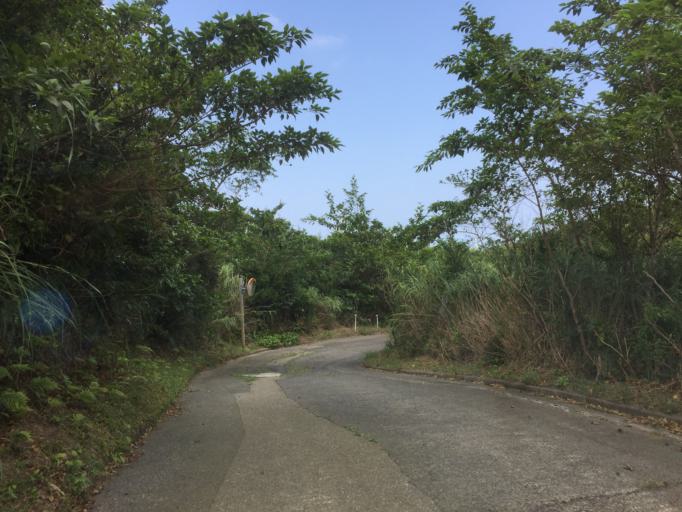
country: JP
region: Shizuoka
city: Shimoda
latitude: 34.0899
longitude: 139.5025
